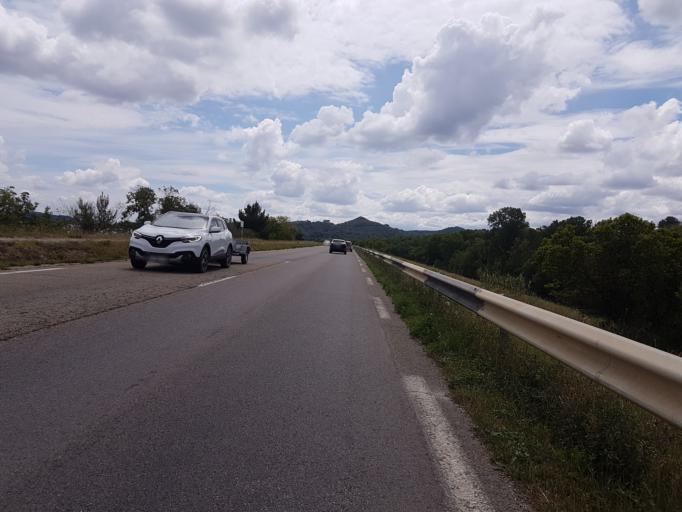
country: FR
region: Languedoc-Roussillon
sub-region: Departement du Gard
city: Vallabregues
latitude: 43.8605
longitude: 4.6182
